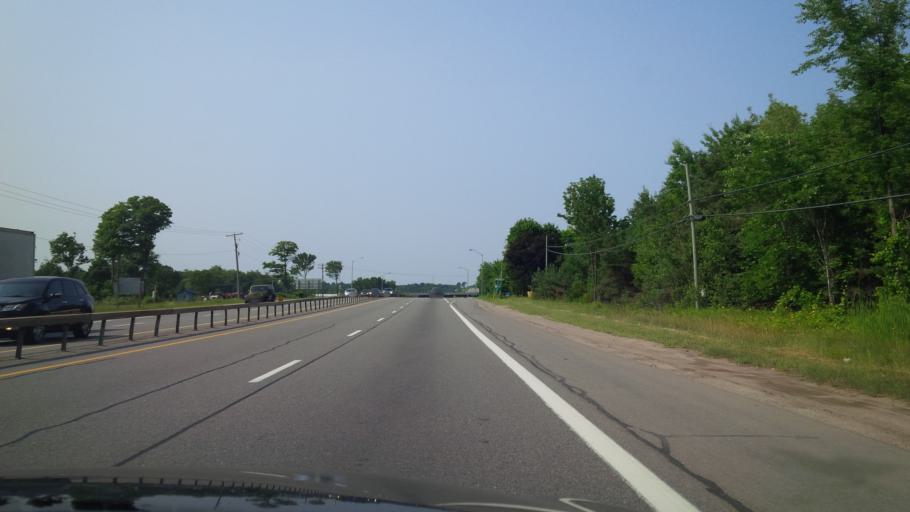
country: CA
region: Ontario
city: Orillia
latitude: 44.5515
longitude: -79.4495
